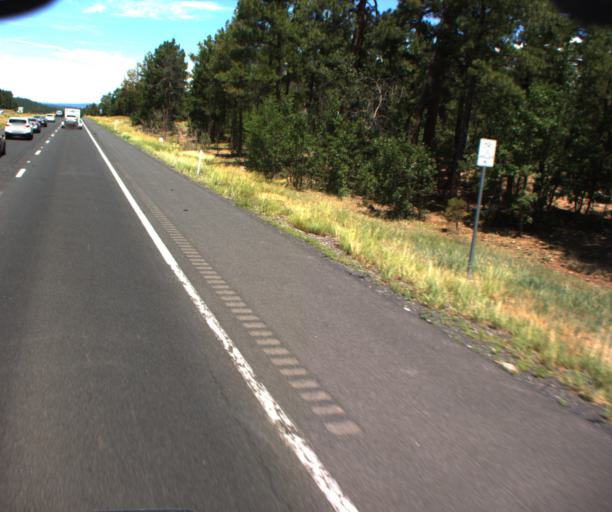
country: US
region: Arizona
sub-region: Coconino County
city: Sedona
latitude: 34.8588
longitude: -111.6122
